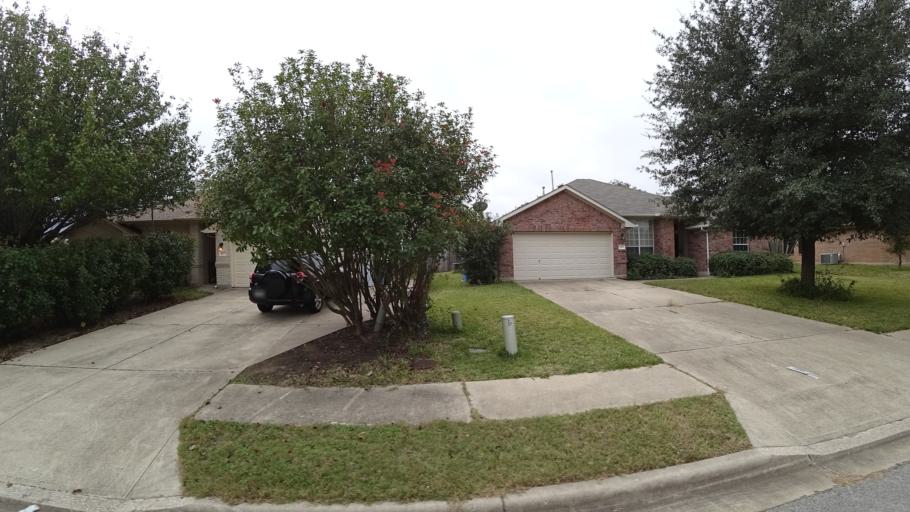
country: US
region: Texas
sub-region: Travis County
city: Pflugerville
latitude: 30.4373
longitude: -97.6038
